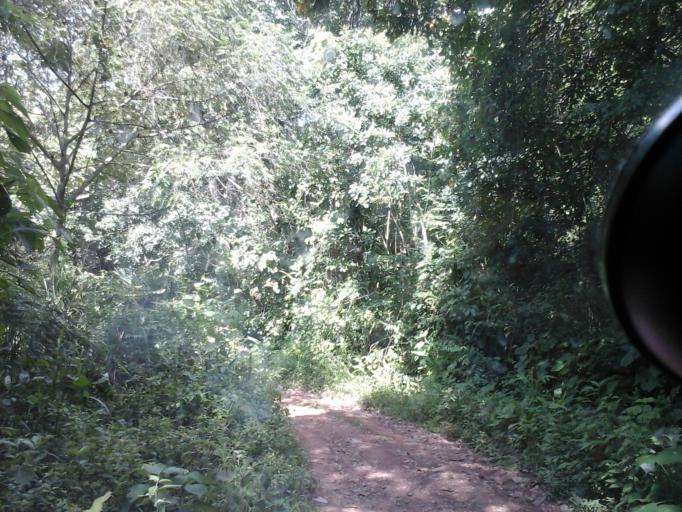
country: CO
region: Cesar
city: San Diego
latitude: 10.2740
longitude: -73.0932
